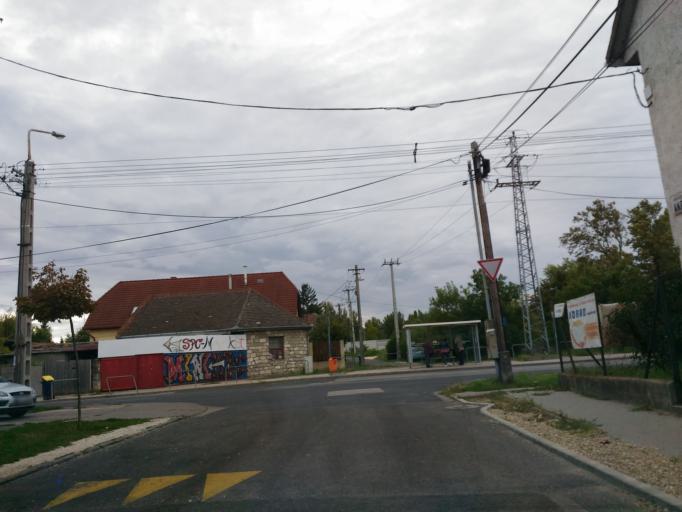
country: HU
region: Pest
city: Halasztelek
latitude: 47.3898
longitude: 18.9777
